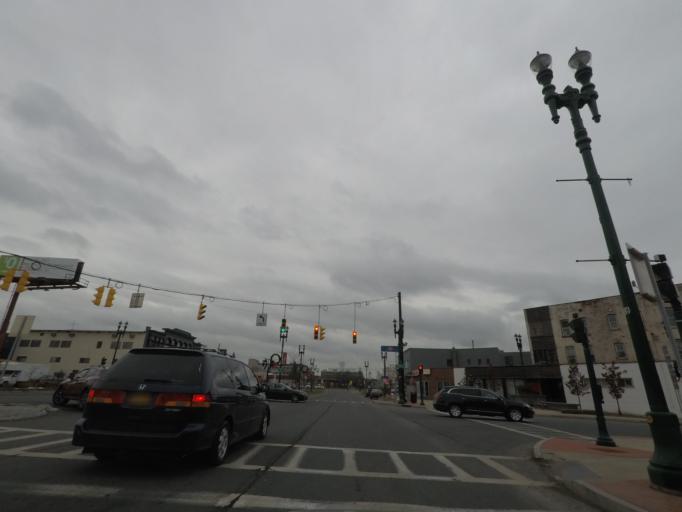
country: US
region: New York
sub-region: Schenectady County
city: Schenectady
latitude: 42.8131
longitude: -73.9465
